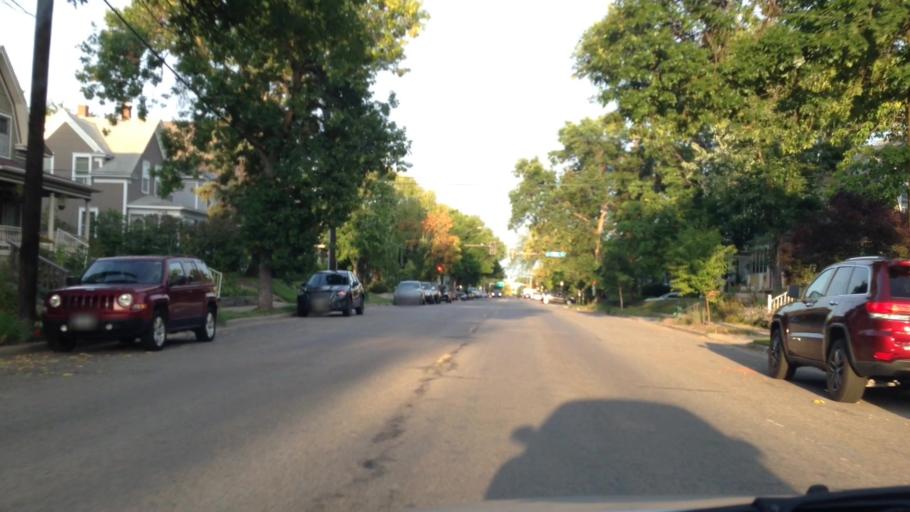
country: US
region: Minnesota
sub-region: Hennepin County
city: Minneapolis
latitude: 44.9377
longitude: -93.2811
